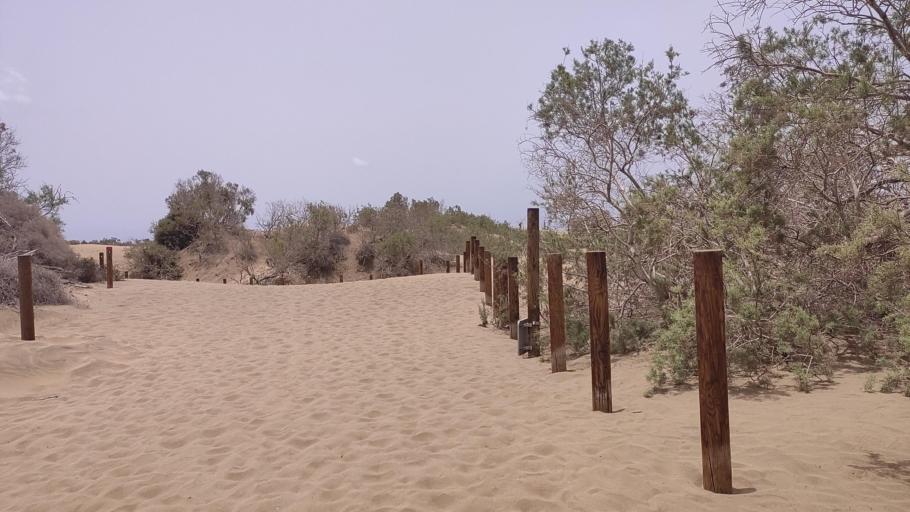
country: ES
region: Canary Islands
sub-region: Provincia de Las Palmas
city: Playa del Ingles
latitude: 27.7406
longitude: -15.5894
